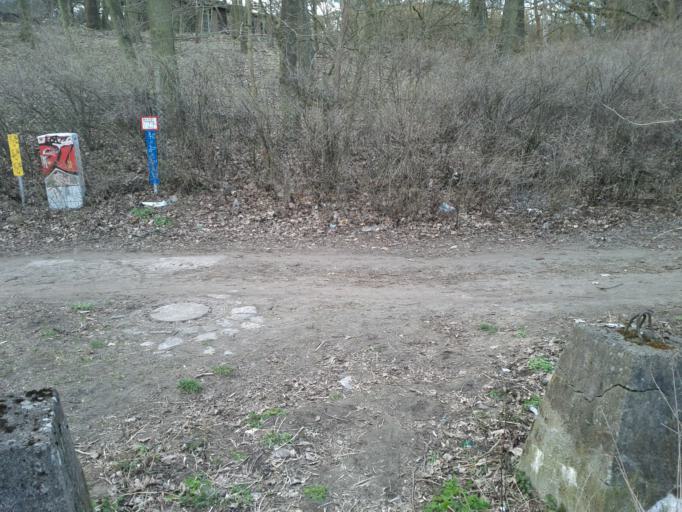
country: DE
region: Brandenburg
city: Woltersdorf
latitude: 52.4608
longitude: 13.7395
